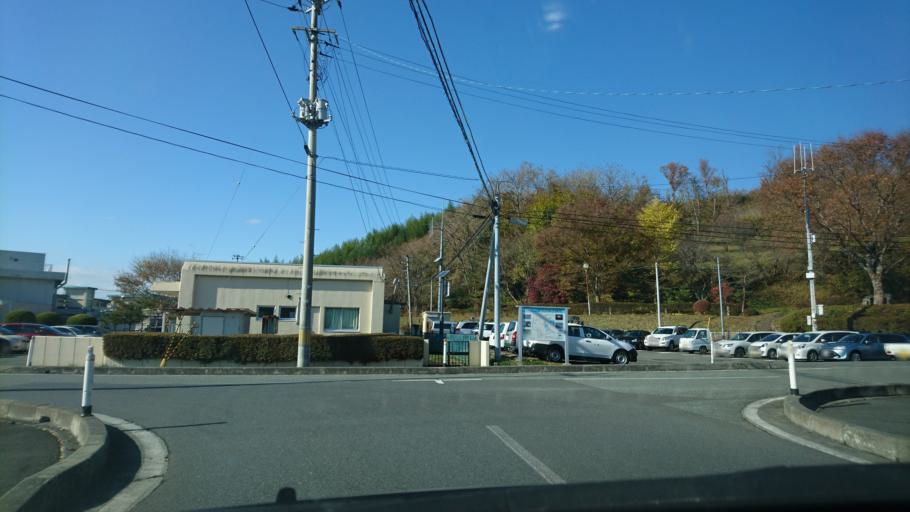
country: JP
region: Iwate
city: Ichinoseki
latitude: 39.0171
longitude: 141.3963
